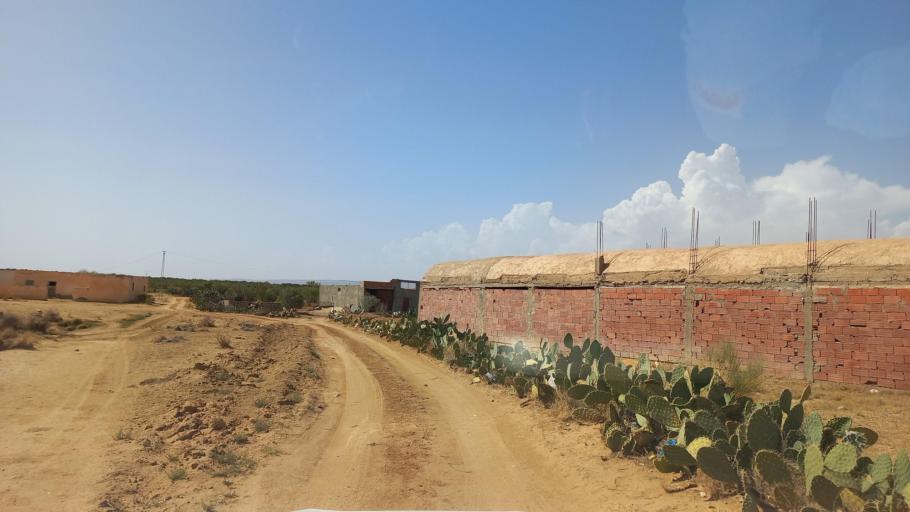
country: TN
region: Al Qasrayn
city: Kasserine
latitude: 35.2106
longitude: 9.0372
